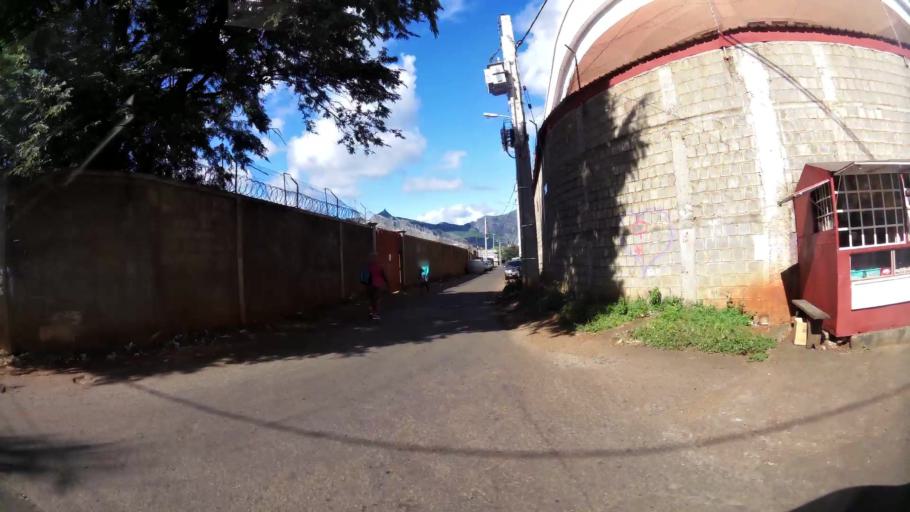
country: MU
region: Pamplemousses
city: Le Hochet
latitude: -20.1432
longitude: 57.5147
